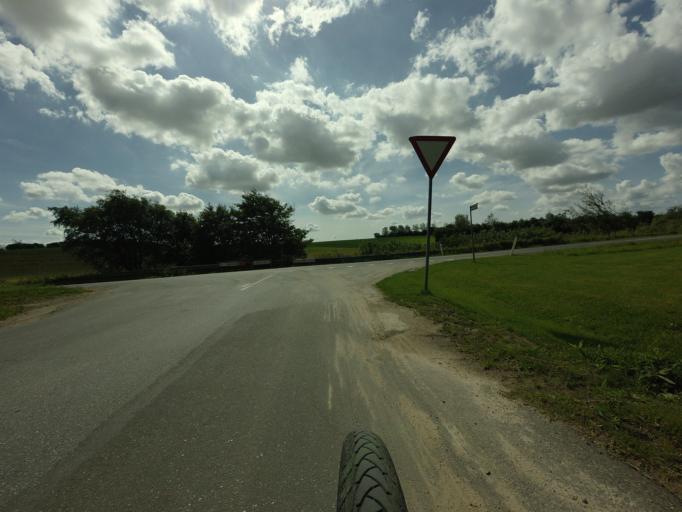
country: DK
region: North Denmark
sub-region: Hjorring Kommune
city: Hjorring
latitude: 57.4529
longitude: 9.9095
